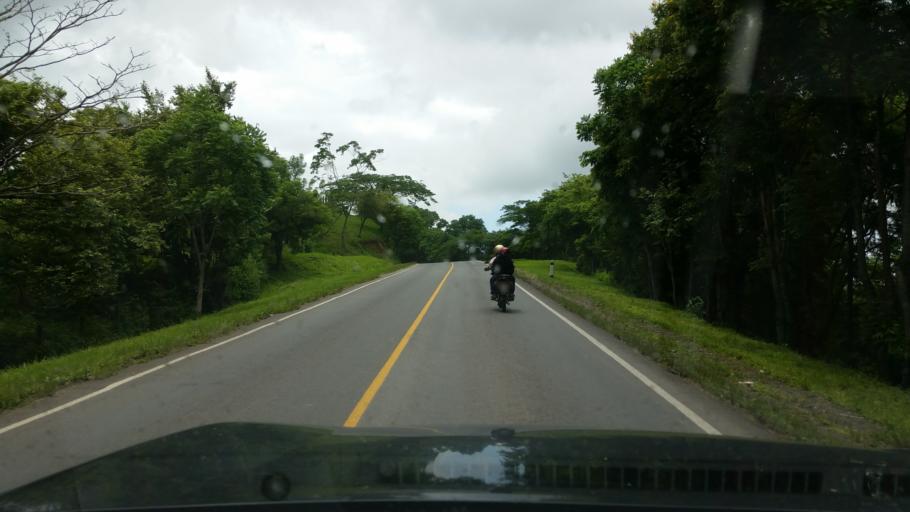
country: NI
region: Matagalpa
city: Matagalpa
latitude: 12.9402
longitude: -85.8802
